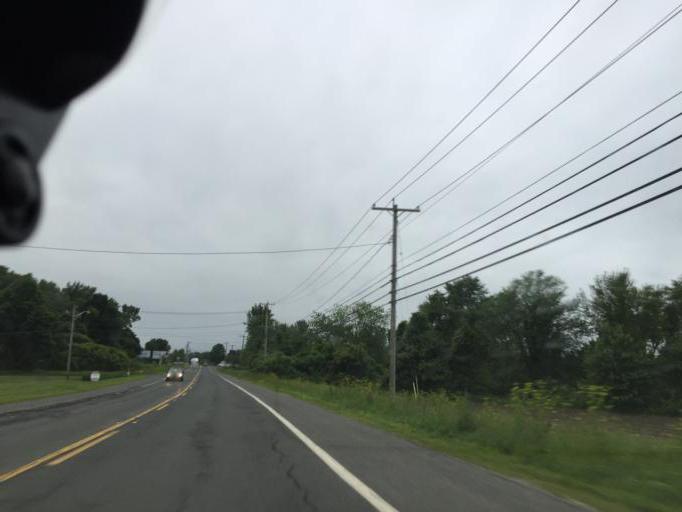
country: US
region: Massachusetts
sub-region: Berkshire County
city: Great Barrington
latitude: 42.1623
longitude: -73.3652
